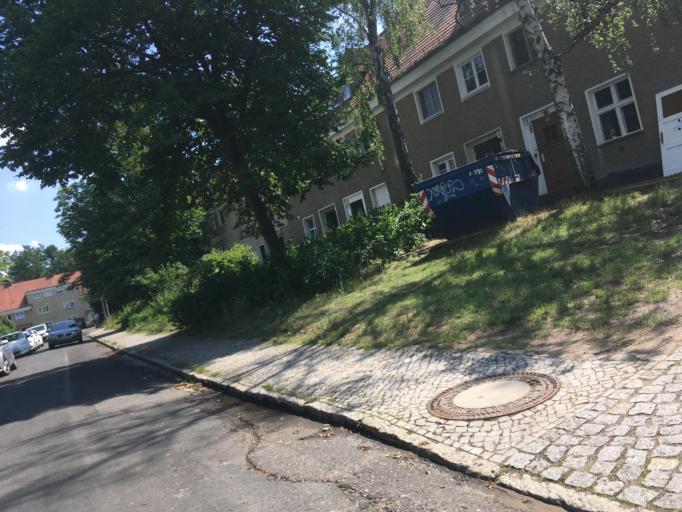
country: DE
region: Berlin
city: Berlin Koepenick
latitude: 52.4601
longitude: 13.5920
